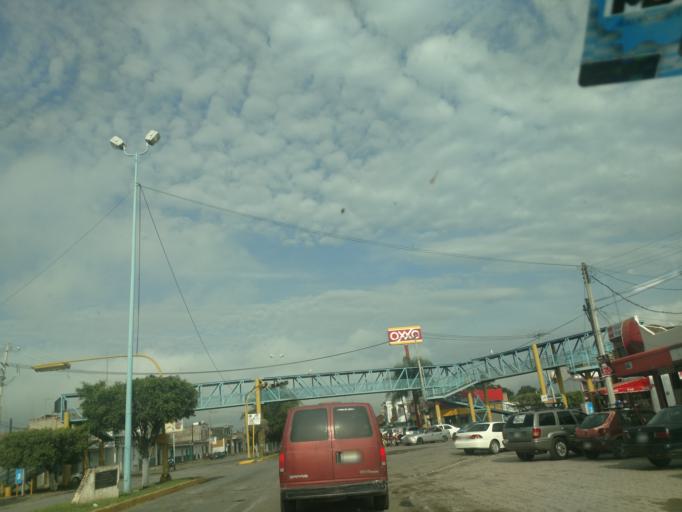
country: MX
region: Jalisco
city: Ameca
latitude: 20.5378
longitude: -104.0413
